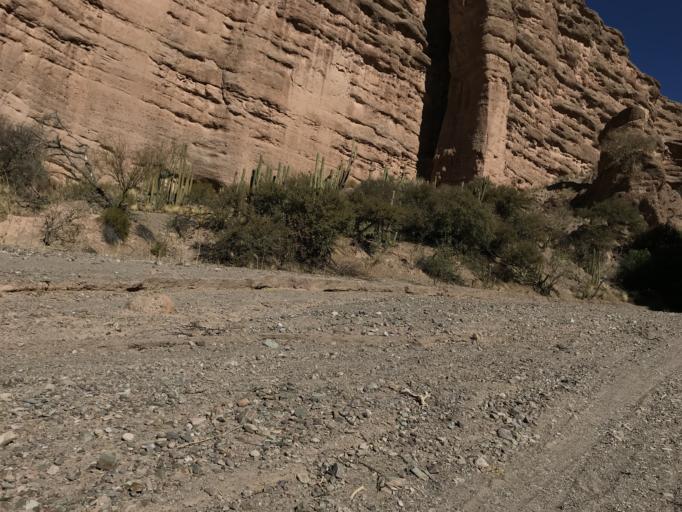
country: BO
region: Potosi
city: Tupiza
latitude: -21.3934
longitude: -65.7537
